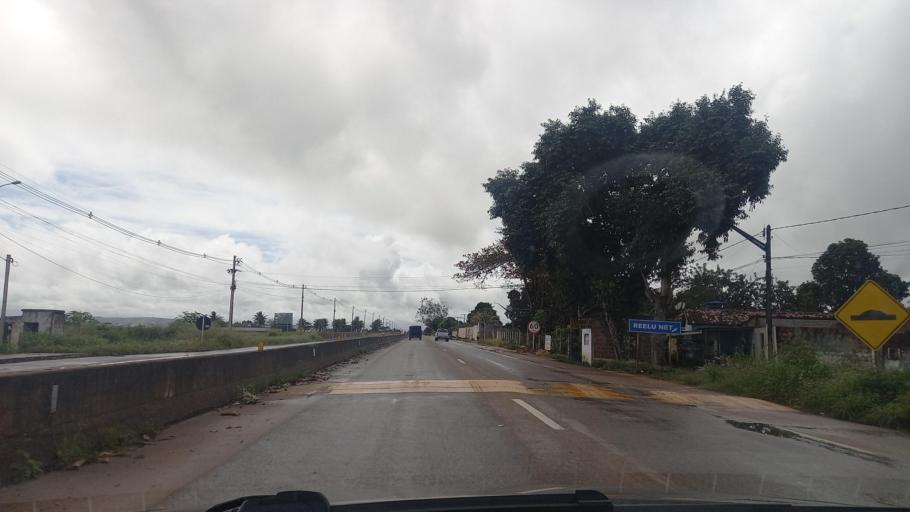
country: BR
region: Alagoas
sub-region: Limoeiro De Anadia
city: Limoeiro de Anadia
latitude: -9.7632
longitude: -36.5326
